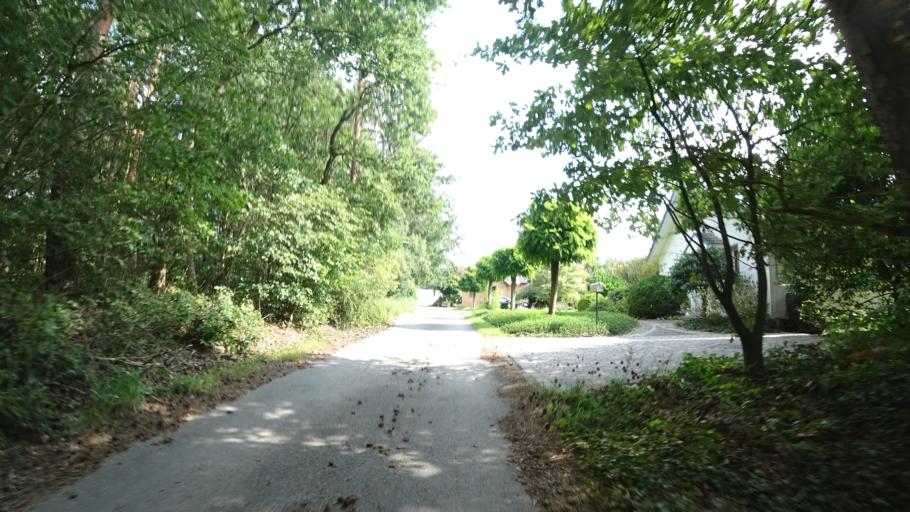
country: DE
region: North Rhine-Westphalia
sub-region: Regierungsbezirk Detmold
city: Guetersloh
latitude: 51.9298
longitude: 8.4160
